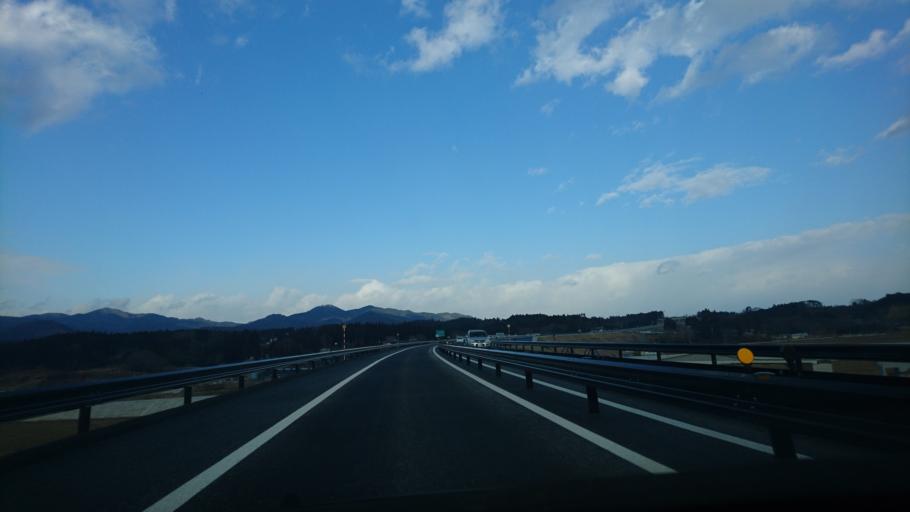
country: JP
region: Miyagi
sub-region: Oshika Gun
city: Onagawa Cho
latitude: 38.7717
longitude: 141.4971
